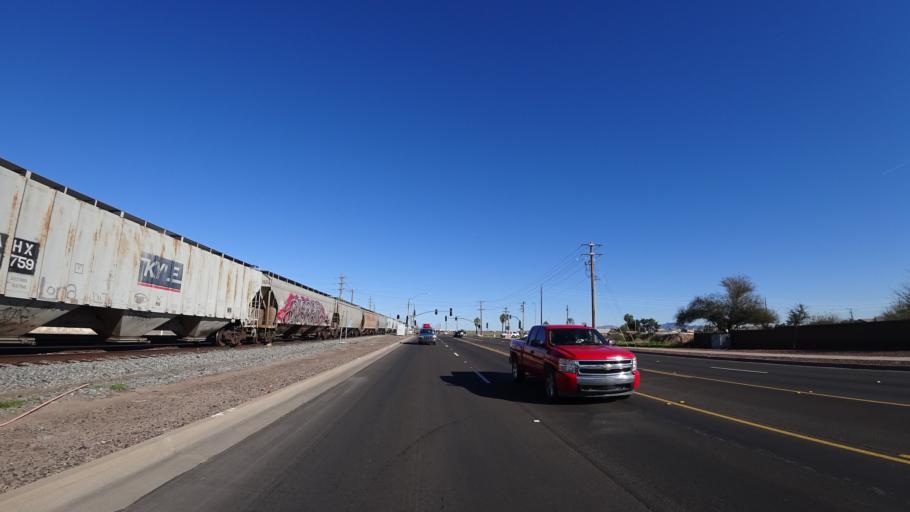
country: US
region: Arizona
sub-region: Maricopa County
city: Tolleson
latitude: 33.4355
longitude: -112.2909
